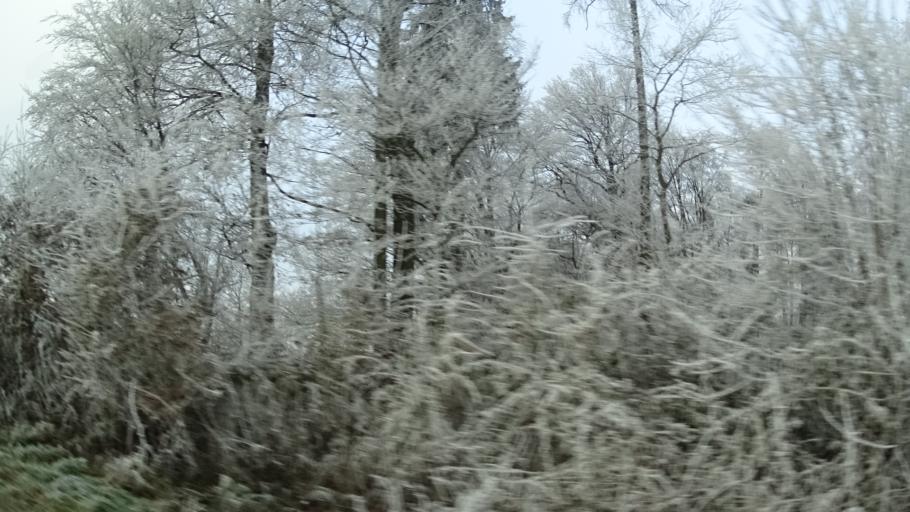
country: DE
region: Hesse
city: Lutzelbach
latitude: 49.7624
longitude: 8.7481
